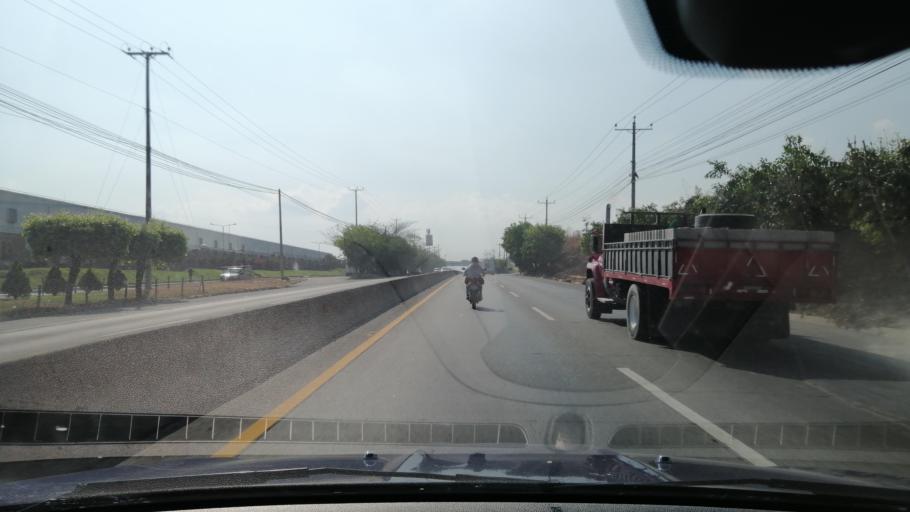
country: SV
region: La Libertad
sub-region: Distrito de Quezaltepeque
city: Quezaltepeque
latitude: 13.8000
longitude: -89.2321
